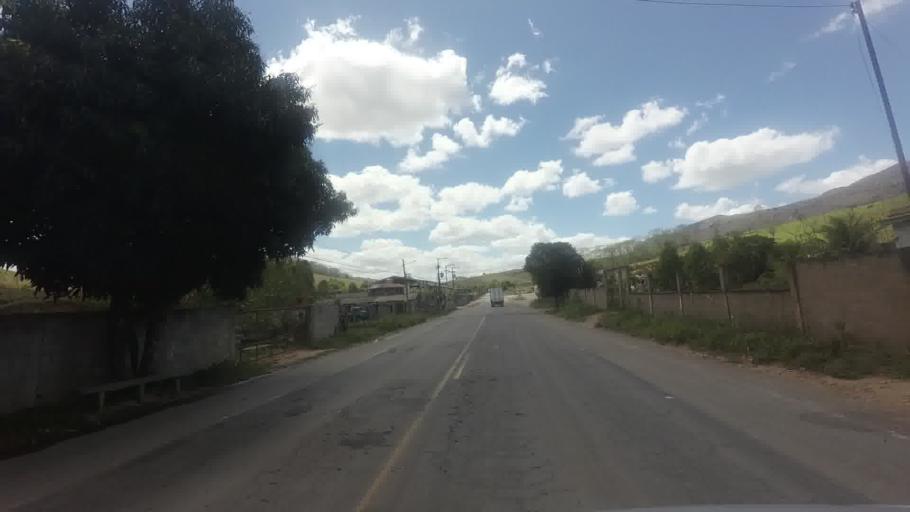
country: BR
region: Rio de Janeiro
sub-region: Santo Antonio De Padua
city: Santo Antonio de Padua
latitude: -21.6393
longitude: -42.2769
